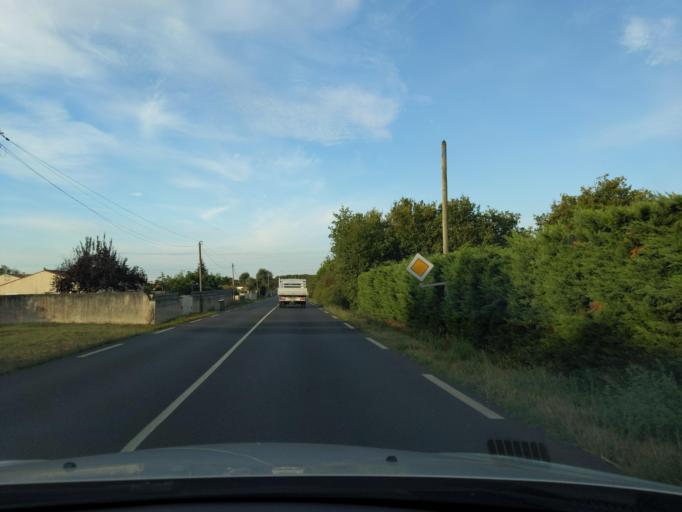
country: FR
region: Poitou-Charentes
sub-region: Departement de la Charente-Maritime
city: Saint-Trojan-les-Bains
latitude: 45.8759
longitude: -1.2209
